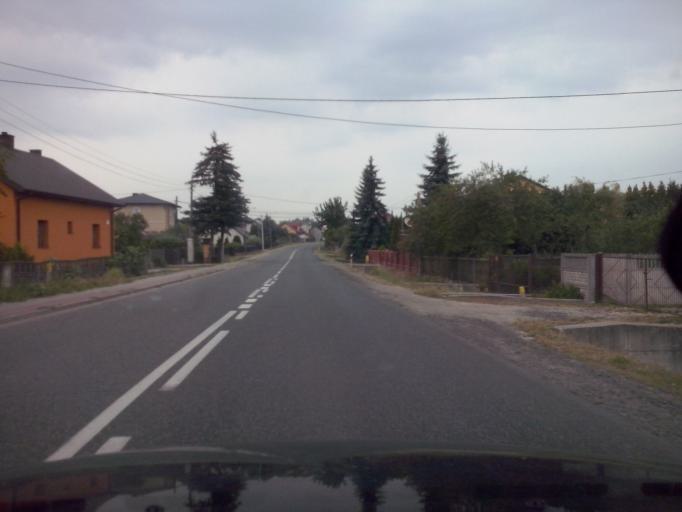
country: PL
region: Swietokrzyskie
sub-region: Powiat kielecki
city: Brzeziny
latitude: 50.7754
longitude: 20.5660
